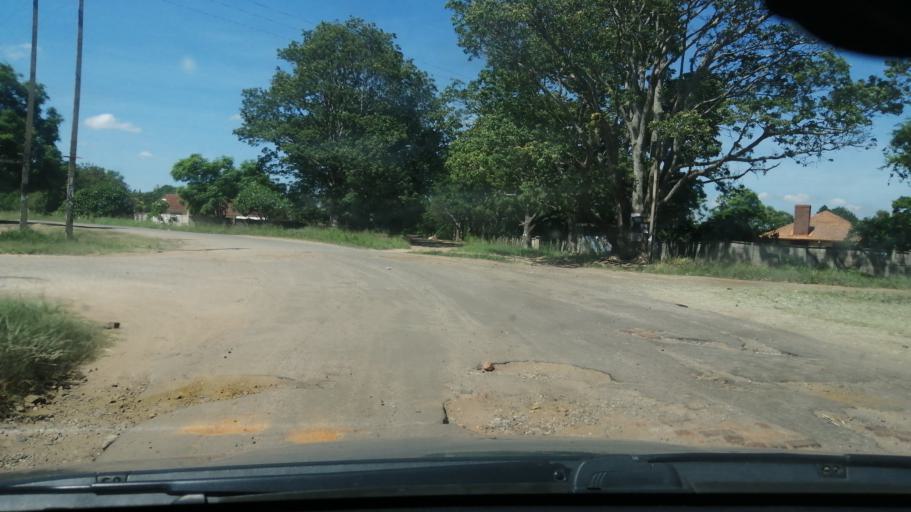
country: ZW
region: Harare
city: Epworth
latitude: -17.8223
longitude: 31.1265
